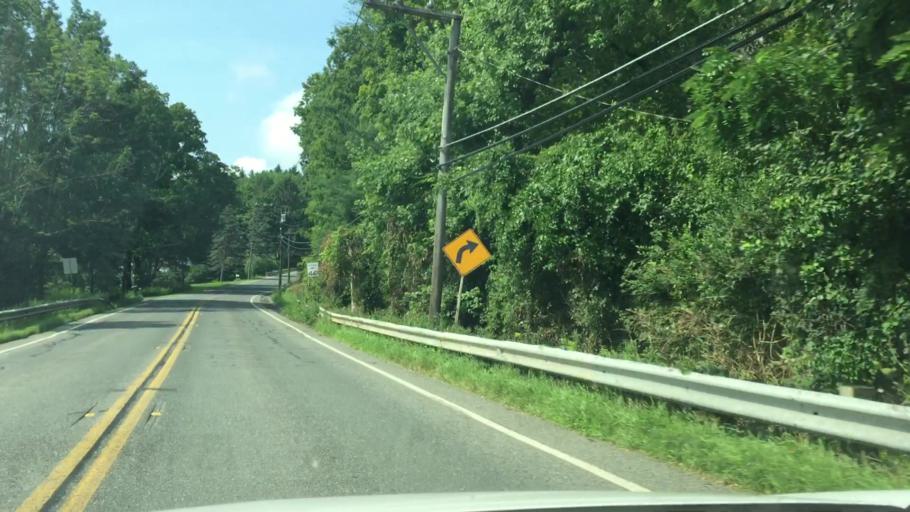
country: US
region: Massachusetts
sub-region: Berkshire County
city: Richmond
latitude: 42.4089
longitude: -73.3508
